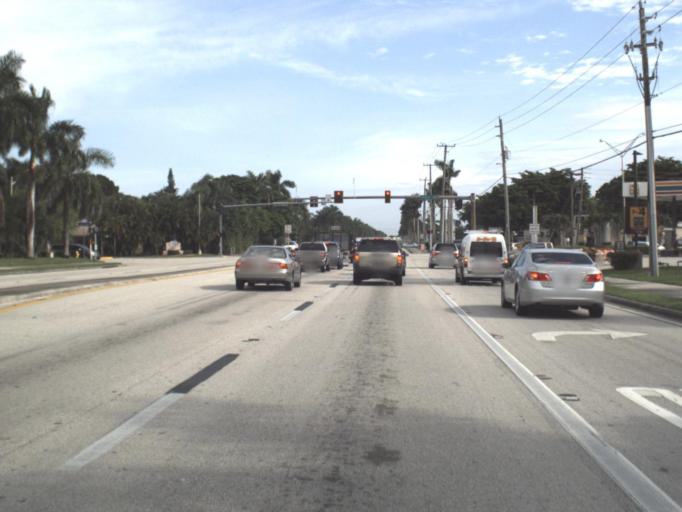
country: US
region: Florida
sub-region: Lee County
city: McGregor
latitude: 26.5447
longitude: -81.9147
